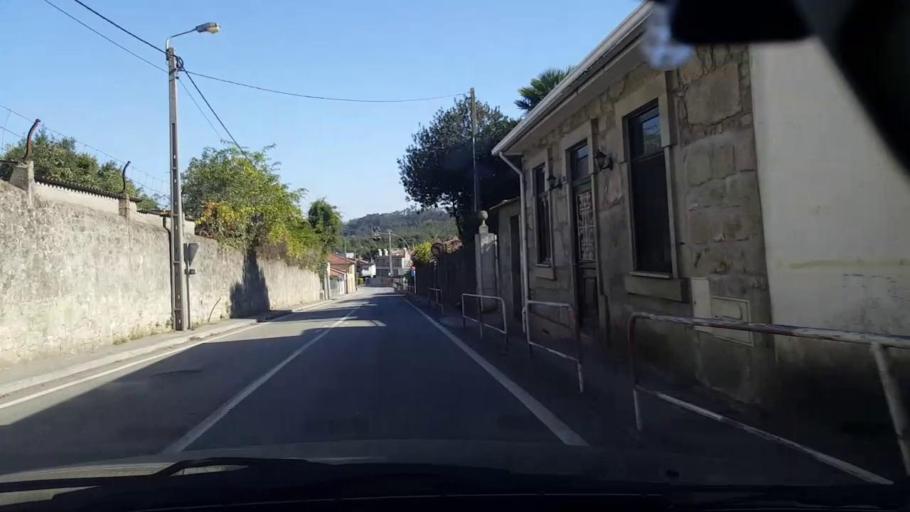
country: PT
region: Porto
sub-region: Vila do Conde
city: Arvore
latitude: 41.3379
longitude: -8.6809
